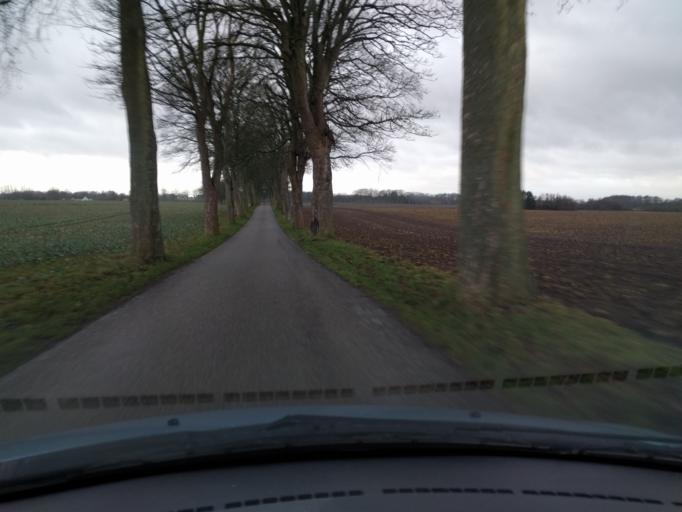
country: DK
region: South Denmark
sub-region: Kerteminde Kommune
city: Langeskov
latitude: 55.3571
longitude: 10.5502
